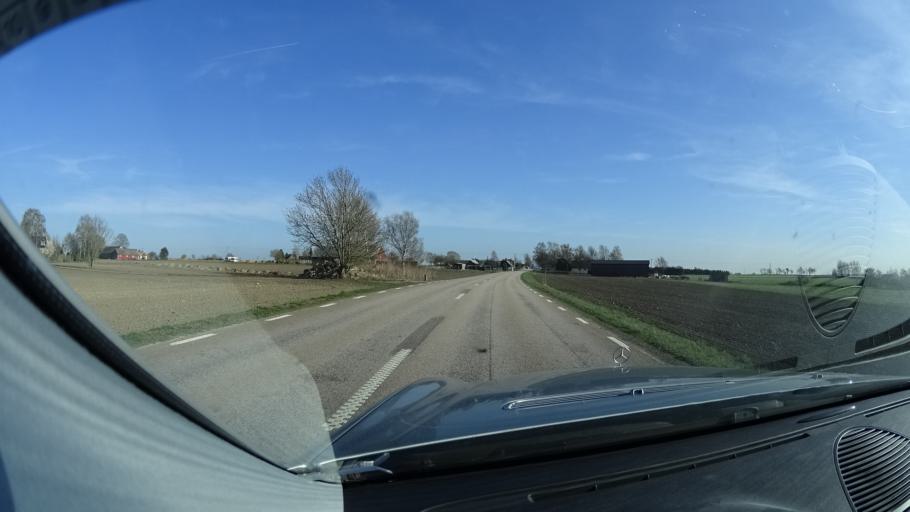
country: SE
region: Skane
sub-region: Landskrona
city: Asmundtorp
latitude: 55.9672
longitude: 12.9424
